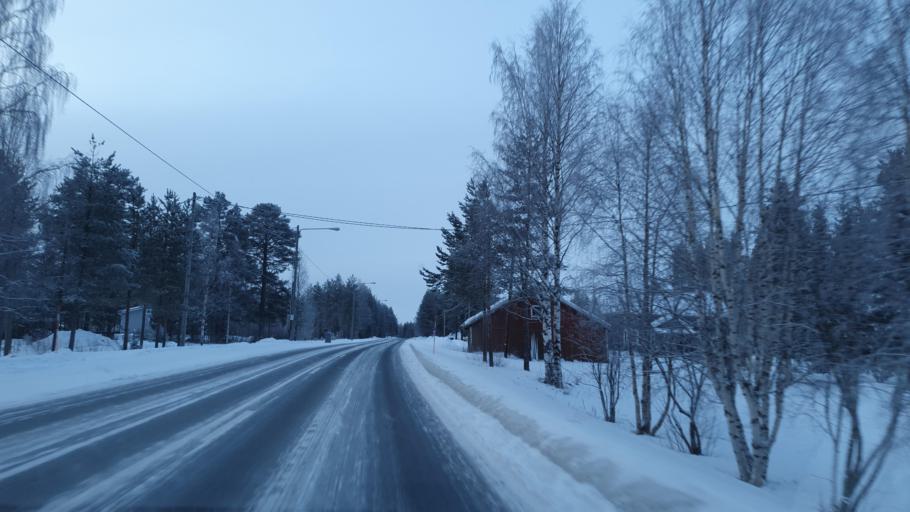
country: FI
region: Lapland
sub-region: Torniolaakso
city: Pello
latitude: 66.7195
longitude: 23.9110
